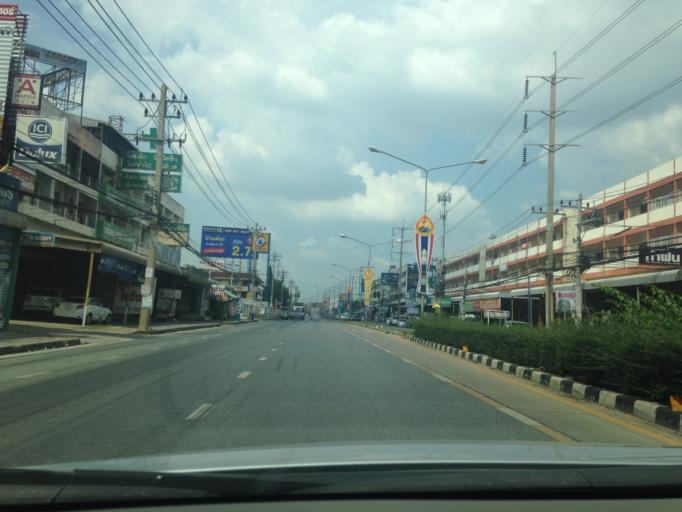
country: TH
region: Pathum Thani
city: Sam Khok
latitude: 14.0420
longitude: 100.5252
